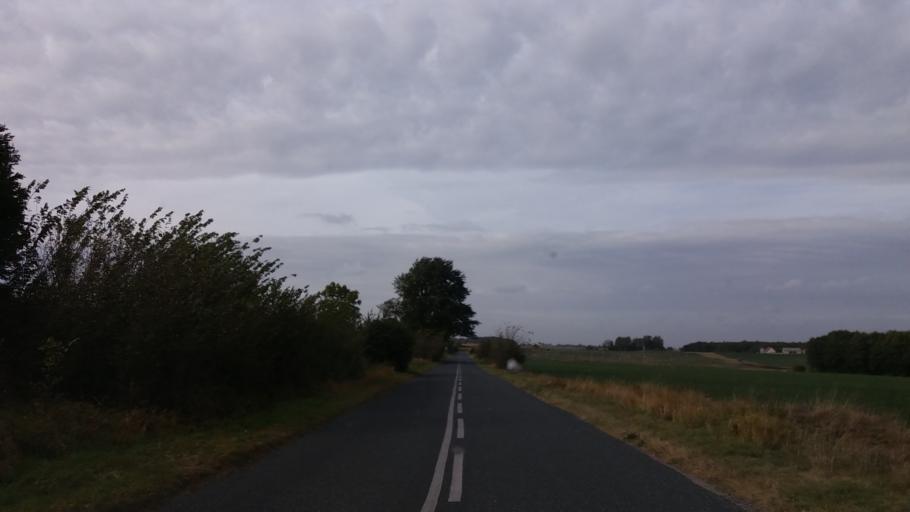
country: PL
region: West Pomeranian Voivodeship
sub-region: Powiat choszczenski
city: Krzecin
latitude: 53.0364
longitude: 15.4999
